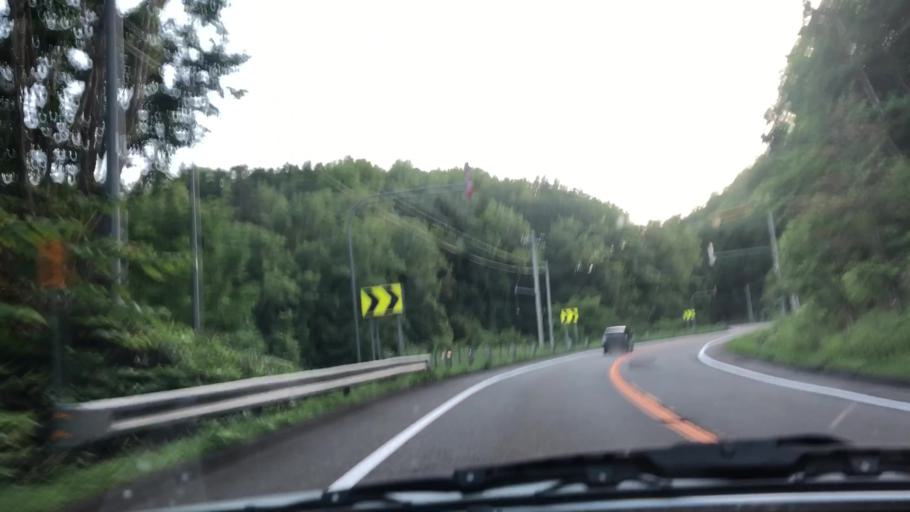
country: JP
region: Hokkaido
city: Shimo-furano
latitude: 42.8913
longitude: 142.2423
